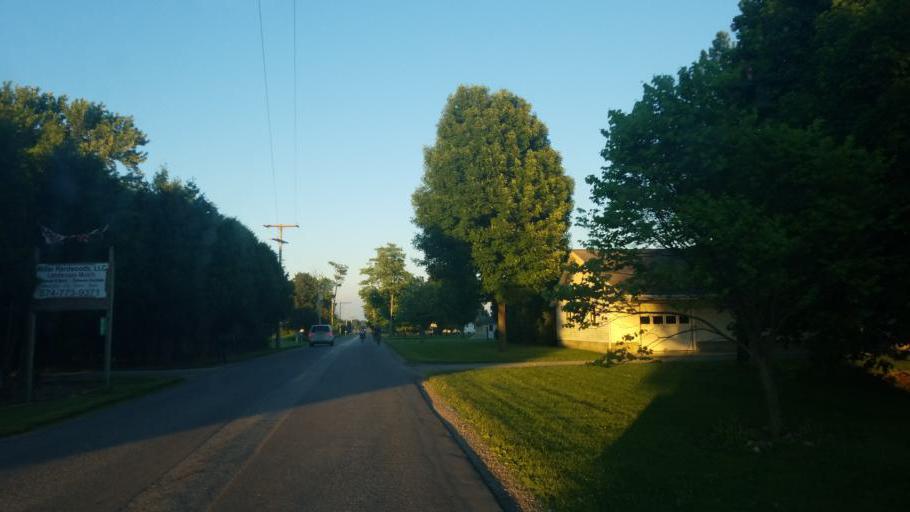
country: US
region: Indiana
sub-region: Elkhart County
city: Nappanee
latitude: 41.4265
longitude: -86.0162
